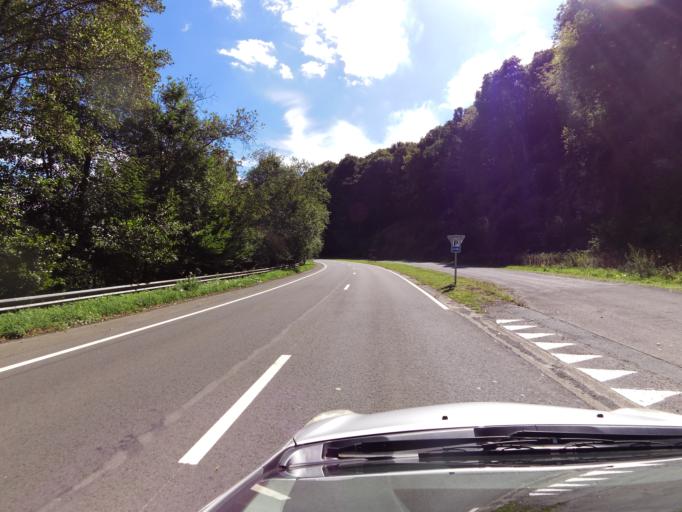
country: BE
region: Wallonia
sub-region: Province du Luxembourg
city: Rendeux
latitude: 50.2083
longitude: 5.5222
